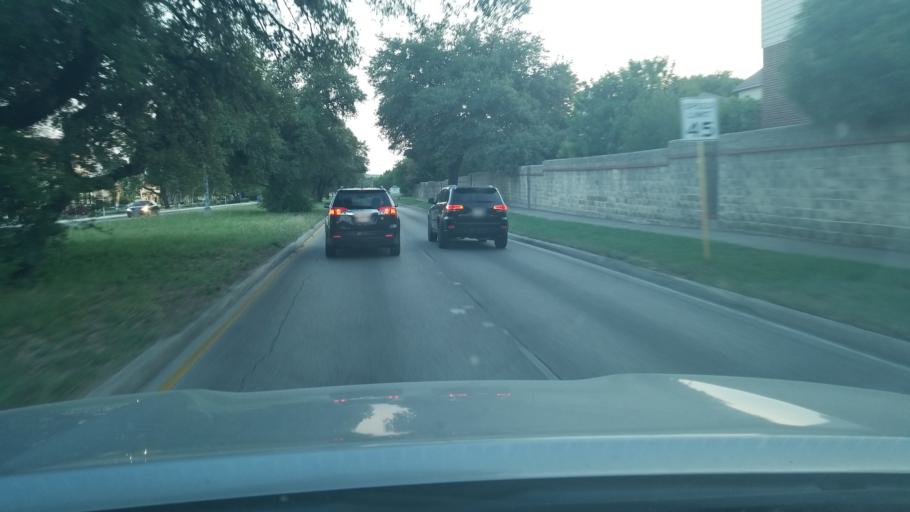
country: US
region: Texas
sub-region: Bexar County
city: Shavano Park
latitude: 29.5849
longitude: -98.5346
